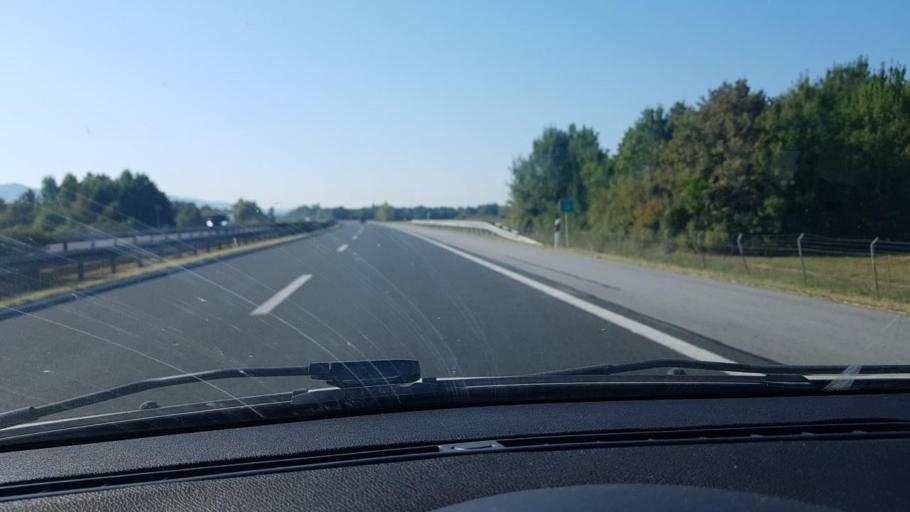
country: HR
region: Zagrebacka
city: Pojatno
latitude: 45.9071
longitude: 15.8203
